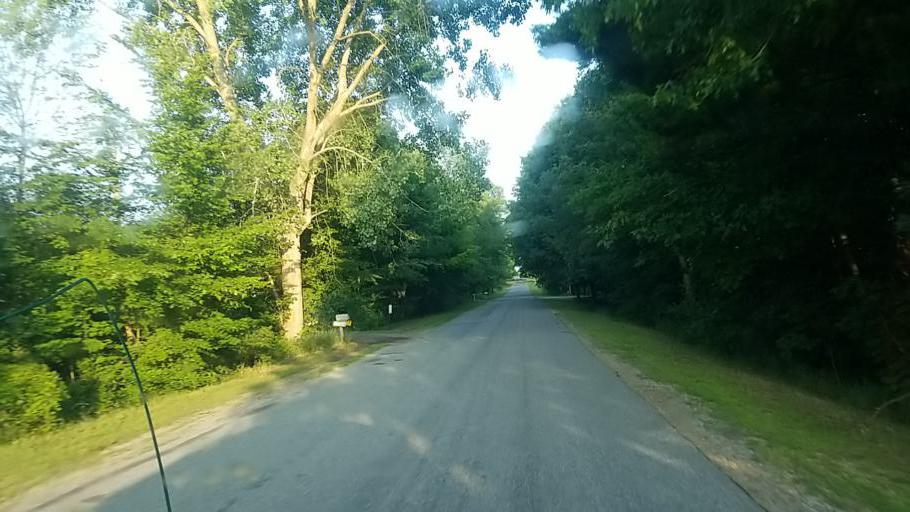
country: US
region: Michigan
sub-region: Muskegon County
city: Twin Lake
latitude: 43.4390
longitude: -86.0865
